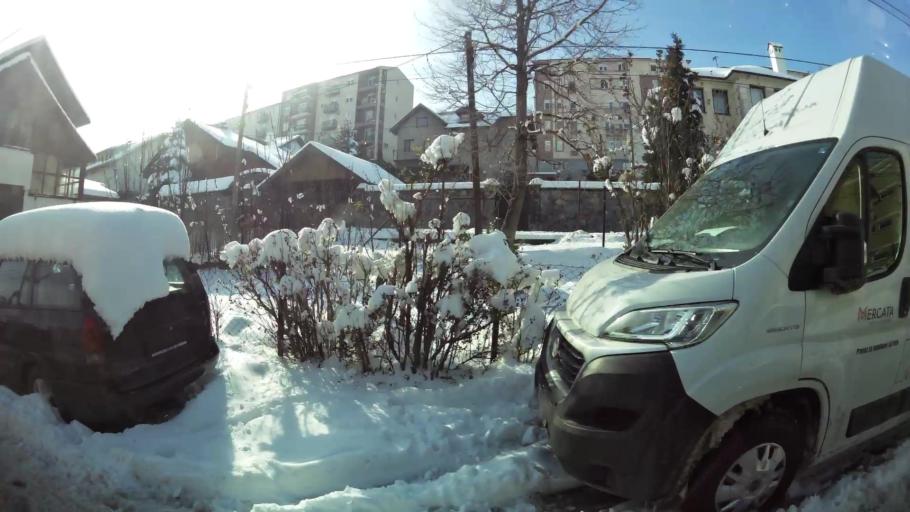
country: RS
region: Central Serbia
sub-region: Belgrade
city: Palilula
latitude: 44.8004
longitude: 20.5248
